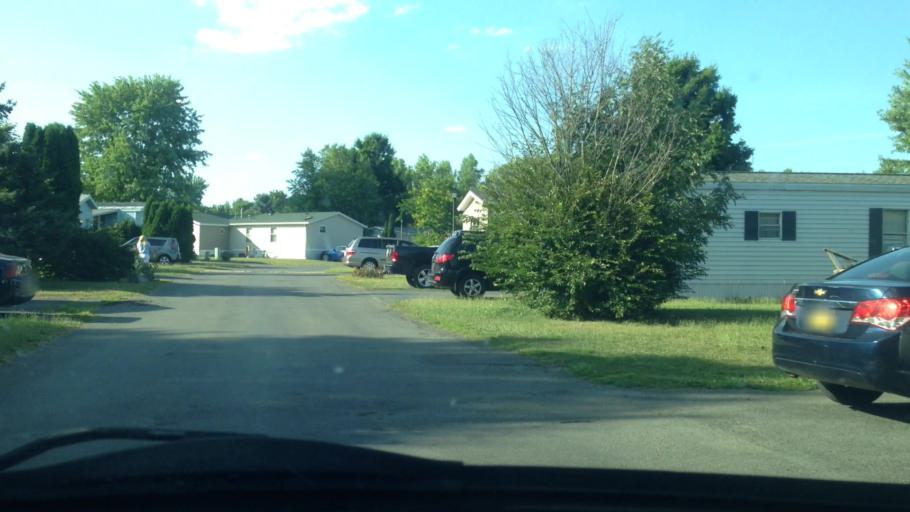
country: US
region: New York
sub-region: Onondaga County
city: Elbridge
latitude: 43.0408
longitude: -76.4135
